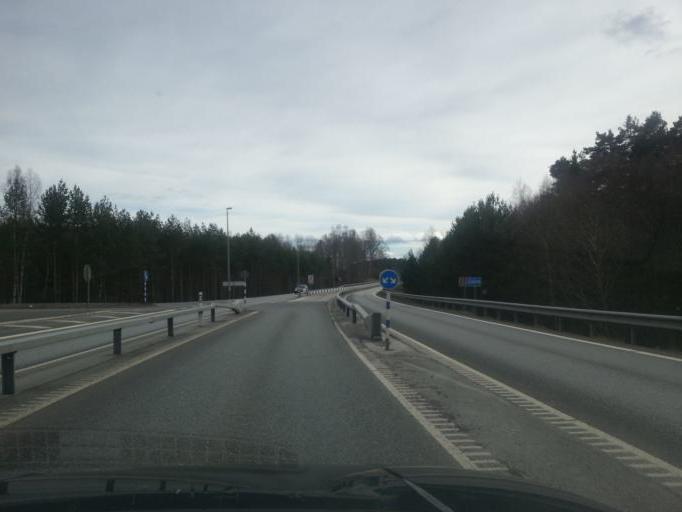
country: SE
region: Joenkoeping
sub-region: Jonkopings Kommun
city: Bankeryd
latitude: 57.8657
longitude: 14.1040
